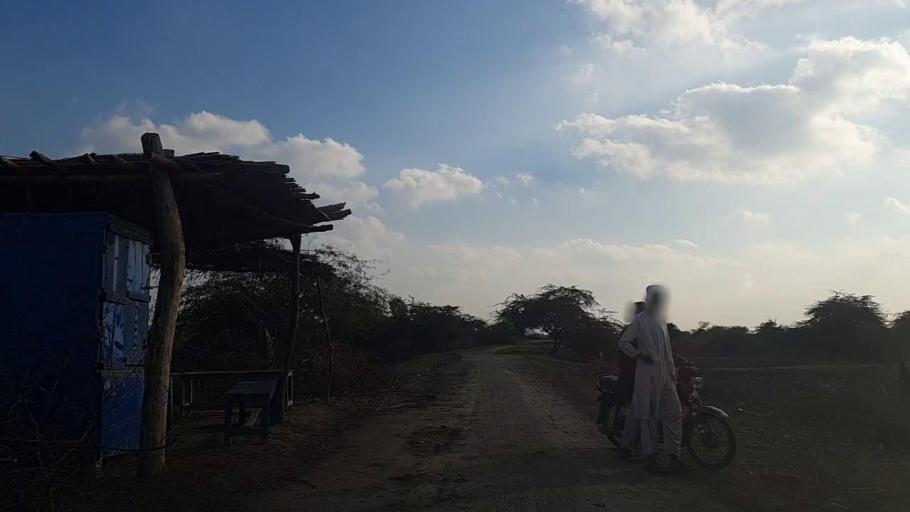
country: PK
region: Sindh
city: Tando Mittha Khan
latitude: 25.9374
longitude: 69.2148
